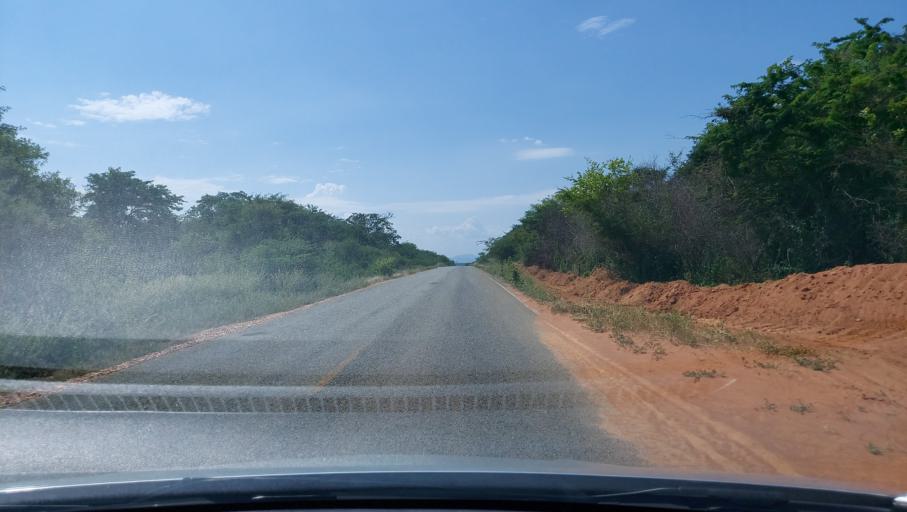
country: BR
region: Bahia
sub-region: Oliveira Dos Brejinhos
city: Beira Rio
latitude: -12.1787
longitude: -42.5427
